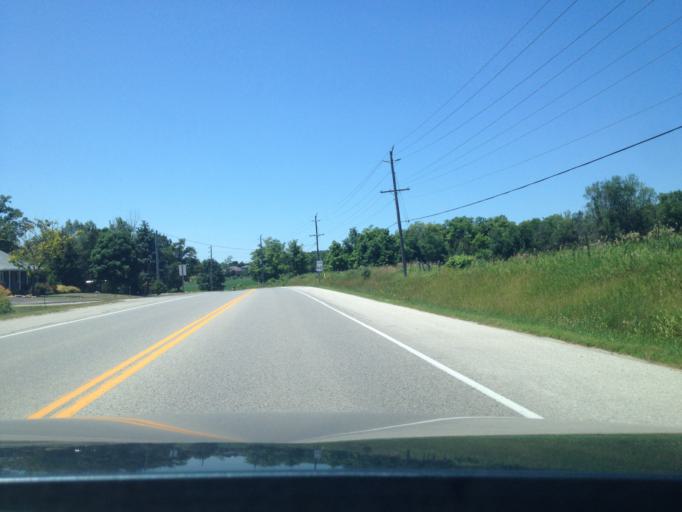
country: CA
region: Ontario
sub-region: Wellington County
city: Guelph
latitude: 43.6928
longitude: -80.4072
